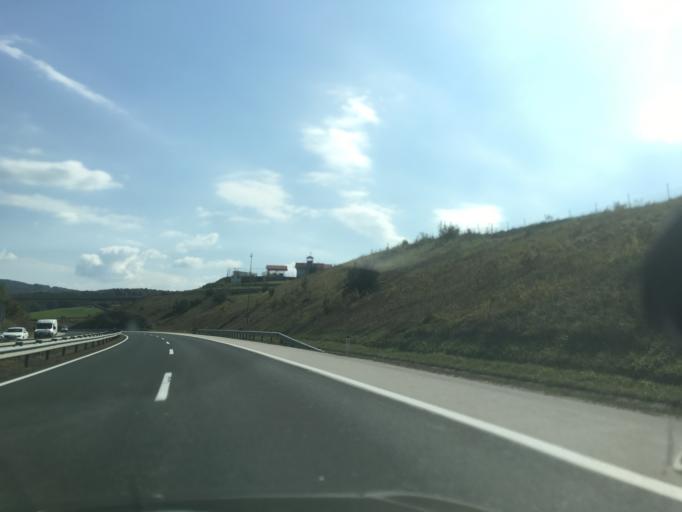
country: SI
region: Trebnje
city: Trebnje
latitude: 45.9131
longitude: 14.9577
